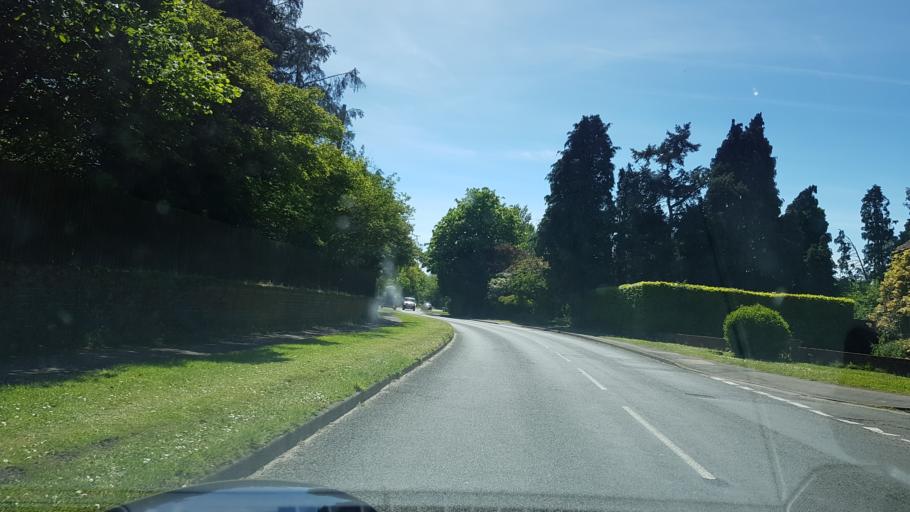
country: GB
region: England
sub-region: Surrey
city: Guildford
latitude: 51.2666
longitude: -0.5685
